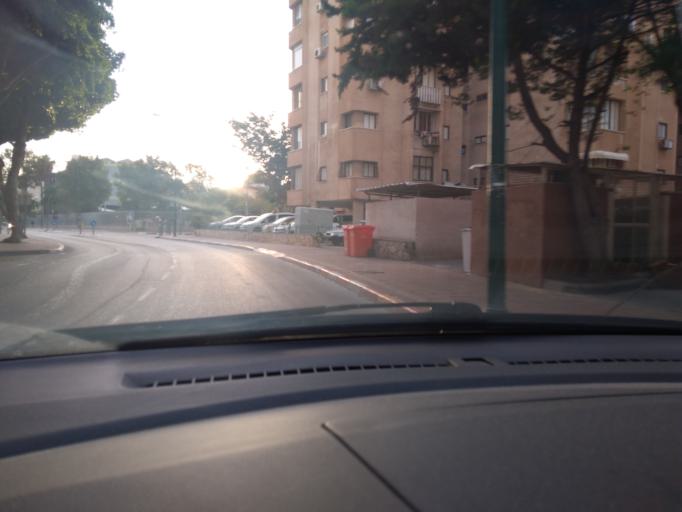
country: IL
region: Central District
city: Netanya
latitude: 32.3354
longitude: 34.8542
